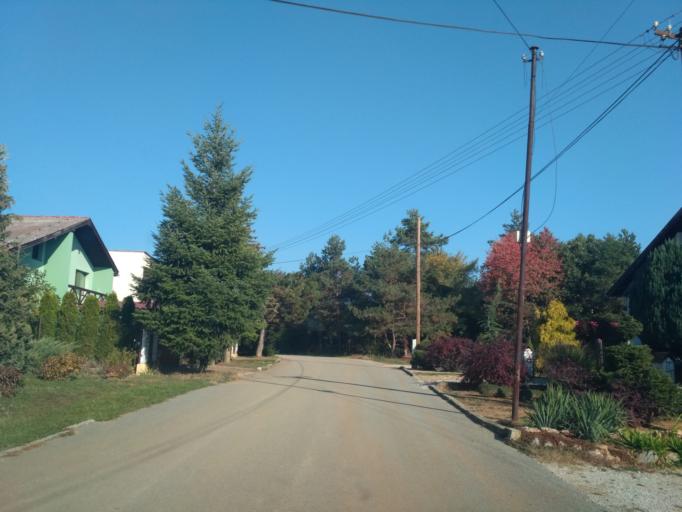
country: SK
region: Kosicky
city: Moldava nad Bodvou
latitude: 48.6172
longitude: 20.9892
